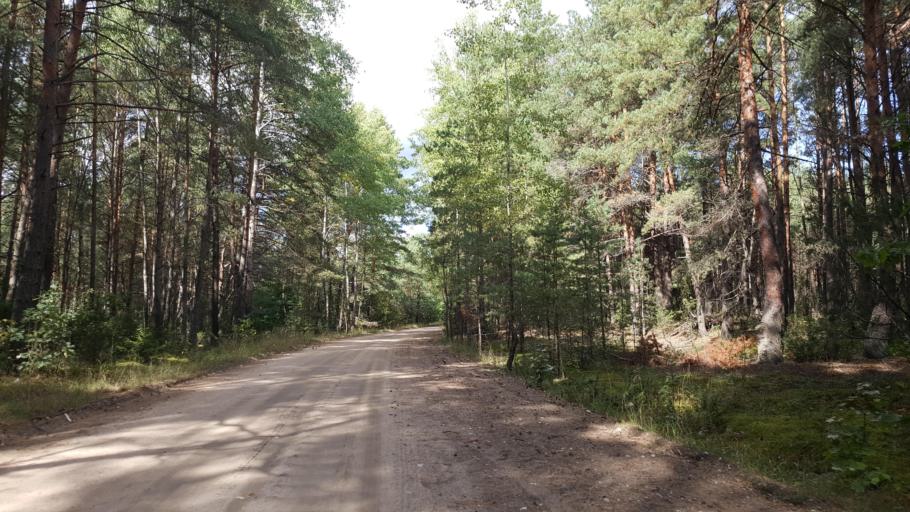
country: BY
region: Brest
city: Kamyanyets
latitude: 52.4365
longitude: 23.9411
